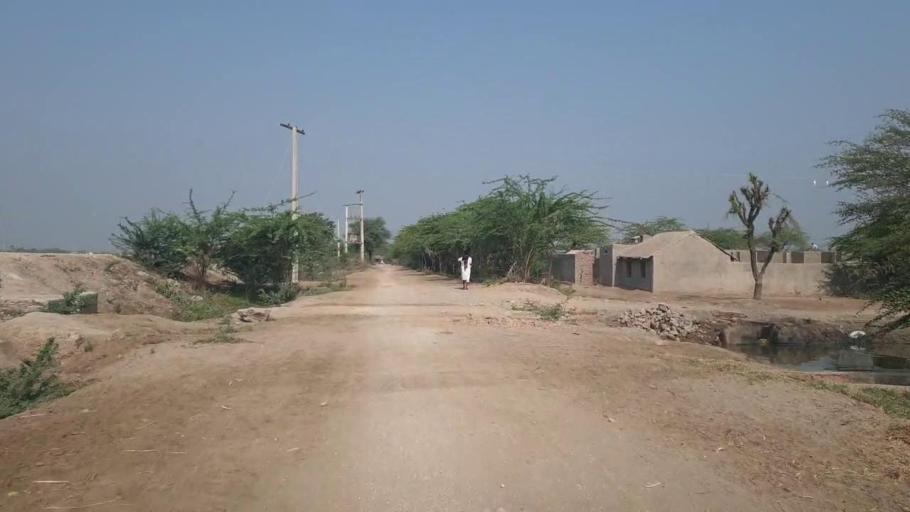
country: PK
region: Sindh
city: Umarkot
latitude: 25.3964
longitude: 69.6995
